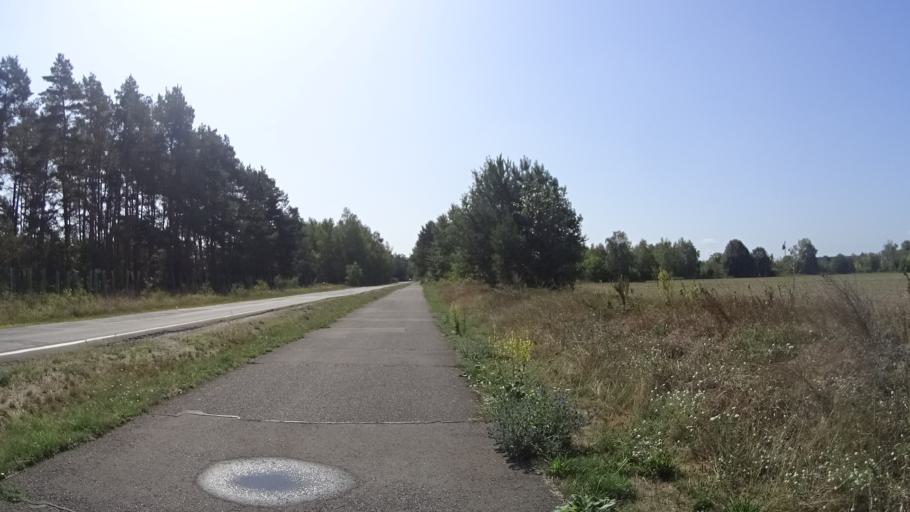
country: DE
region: Brandenburg
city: Cottbus
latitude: 51.7818
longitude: 14.3072
